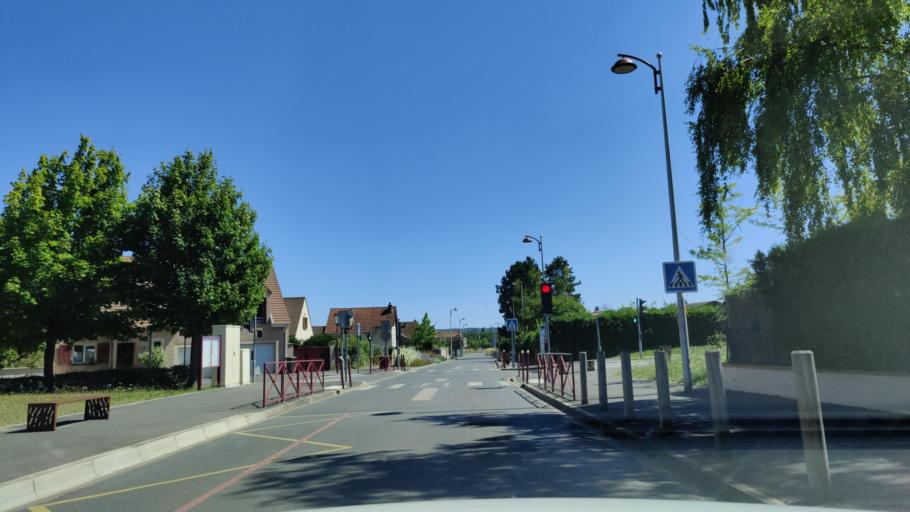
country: FR
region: Ile-de-France
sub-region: Departement de l'Essonne
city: Bruyeres-le-Chatel
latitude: 48.5897
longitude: 2.1891
